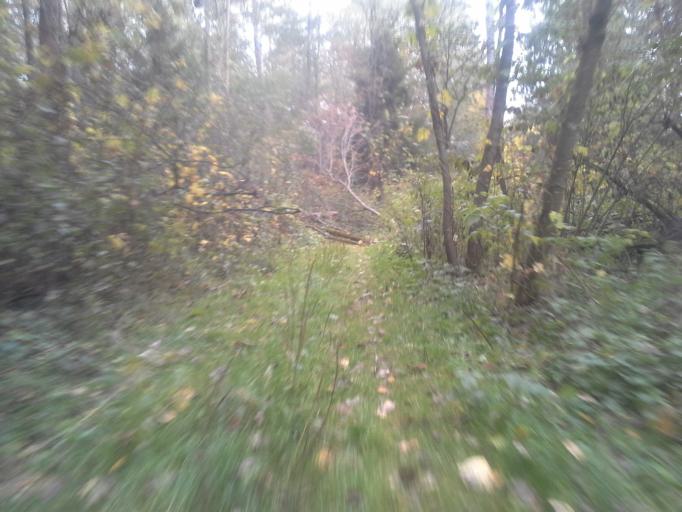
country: RU
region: Moskovskaya
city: Selyatino
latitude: 55.4636
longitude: 36.9543
